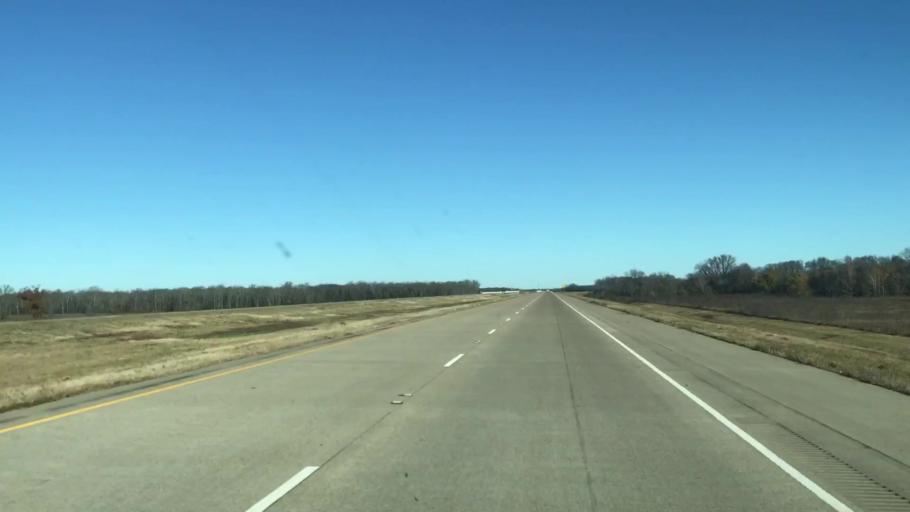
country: US
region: Louisiana
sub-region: Caddo Parish
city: Blanchard
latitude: 32.6186
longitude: -93.8352
